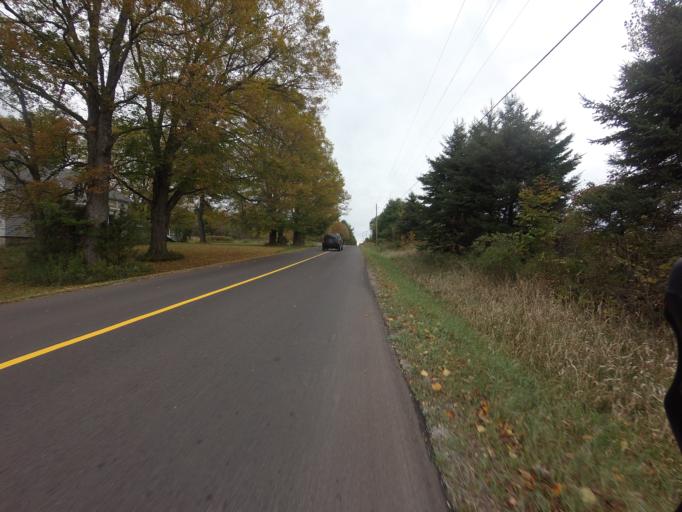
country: CA
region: Ontario
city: Gananoque
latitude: 44.5815
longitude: -76.0603
